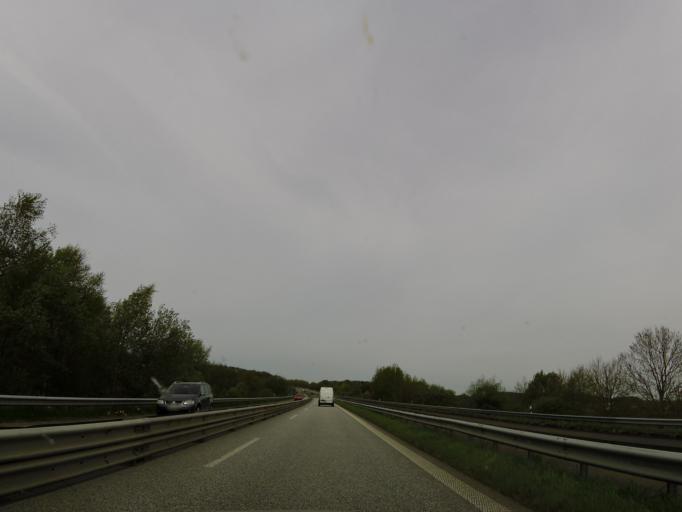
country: DE
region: Schleswig-Holstein
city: Arkebek
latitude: 54.1443
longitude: 9.2456
